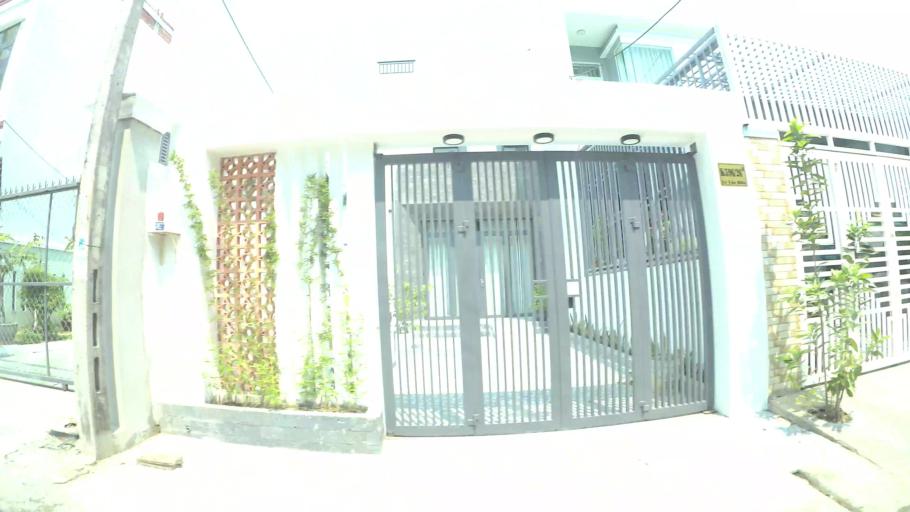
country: VN
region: Da Nang
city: Ngu Hanh Son
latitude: 16.0073
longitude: 108.2560
